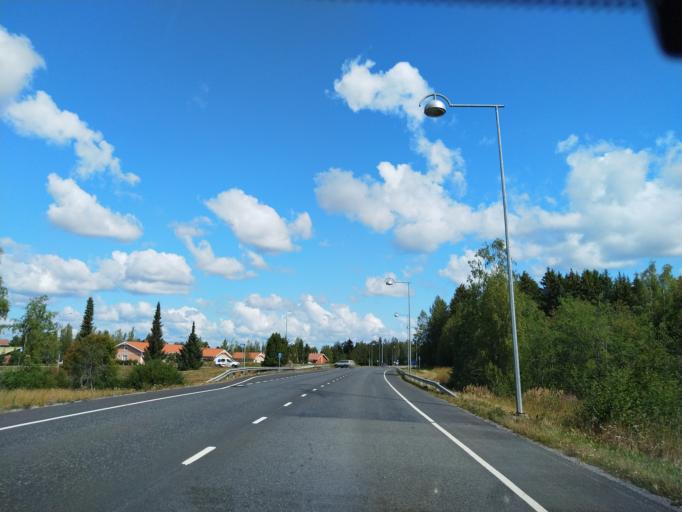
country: FI
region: Satakunta
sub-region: Pori
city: Huittinen
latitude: 61.1710
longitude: 22.7084
